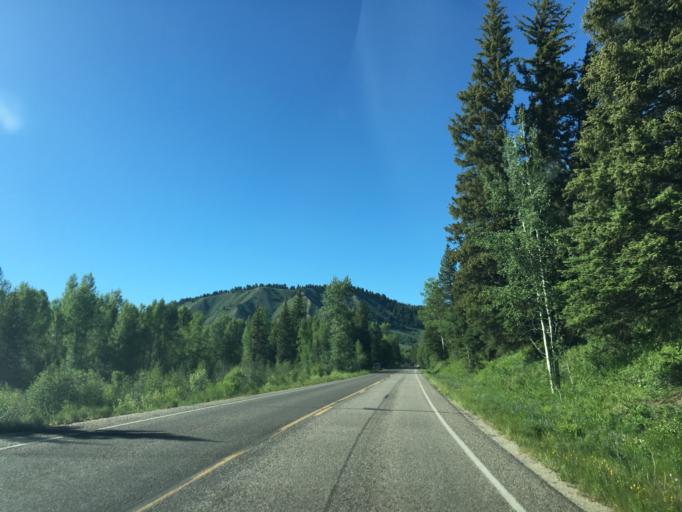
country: US
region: Wyoming
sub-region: Teton County
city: Jackson
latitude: 43.8474
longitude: -110.5175
